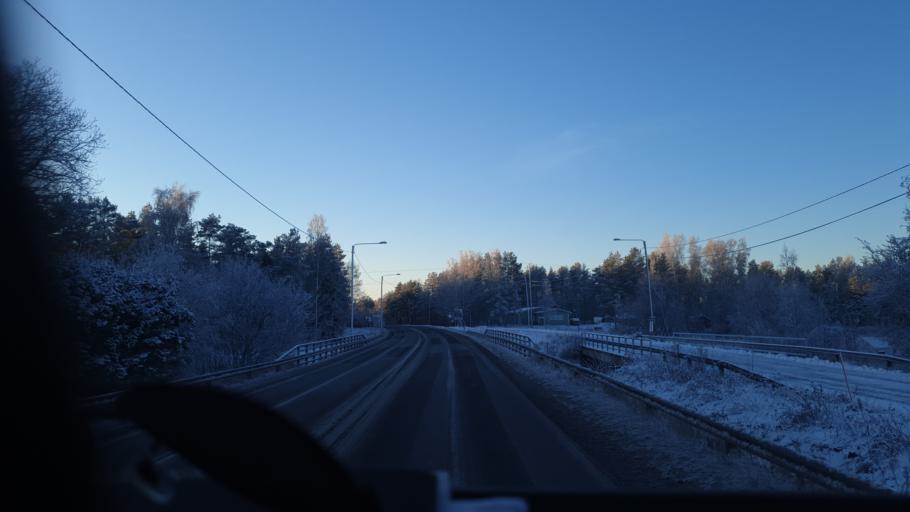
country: FI
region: Northern Ostrobothnia
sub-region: Ylivieska
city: Kalajoki
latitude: 64.2101
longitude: 23.7732
